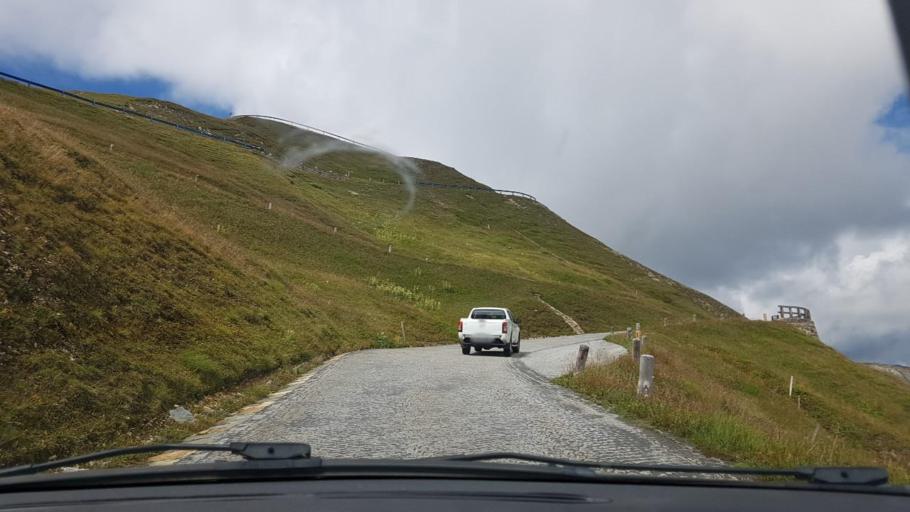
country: AT
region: Carinthia
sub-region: Politischer Bezirk Spittal an der Drau
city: Heiligenblut
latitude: 47.1213
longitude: 12.8309
